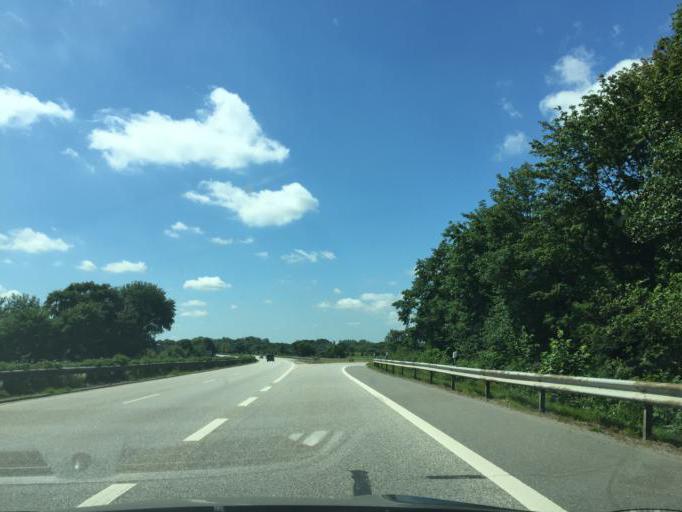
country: DE
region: Schleswig-Holstein
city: Harrislee
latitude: 54.7780
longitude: 9.3807
